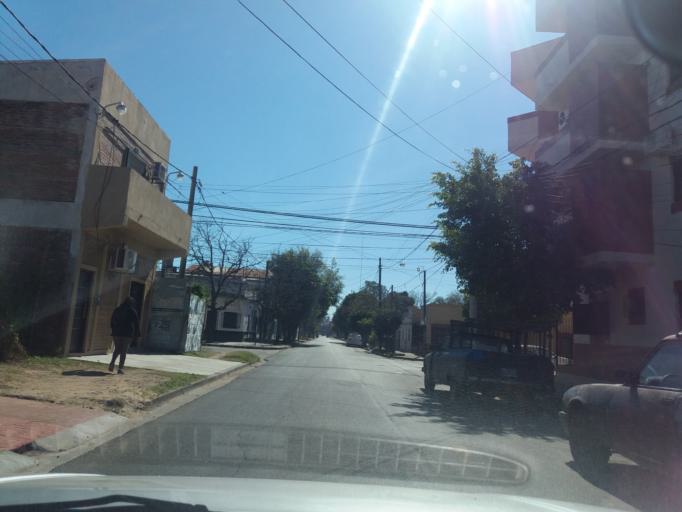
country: AR
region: Corrientes
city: Corrientes
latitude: -27.4788
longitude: -58.8435
